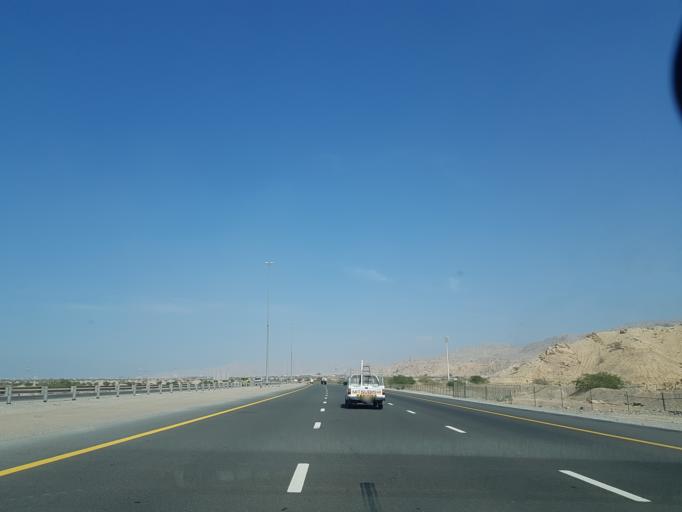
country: AE
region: Ra's al Khaymah
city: Ras al-Khaimah
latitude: 25.7248
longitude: 56.0120
